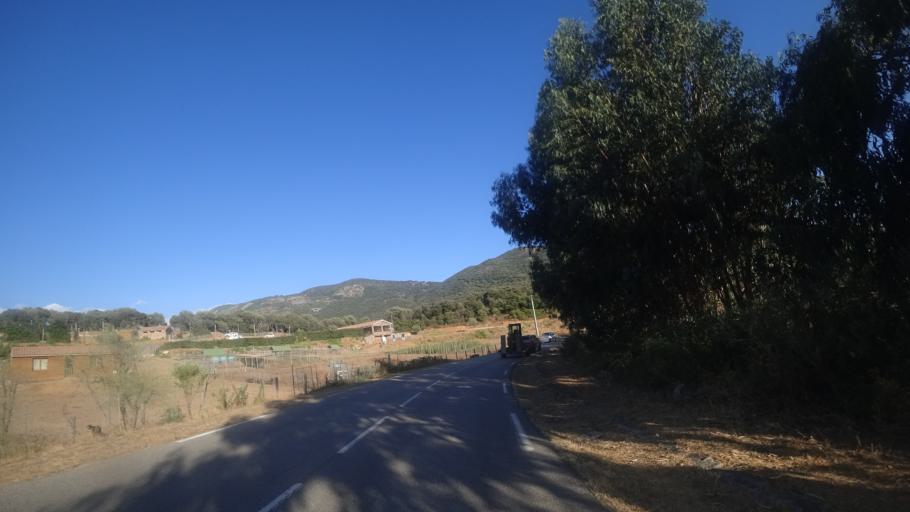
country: FR
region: Corsica
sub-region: Departement de la Corse-du-Sud
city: Cargese
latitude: 42.1585
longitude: 8.6056
